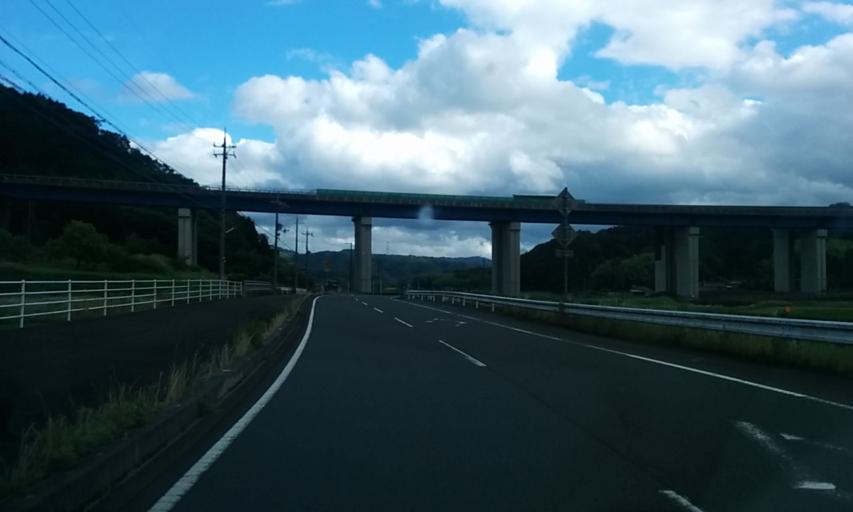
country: JP
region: Kyoto
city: Ayabe
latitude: 35.3488
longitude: 135.2879
